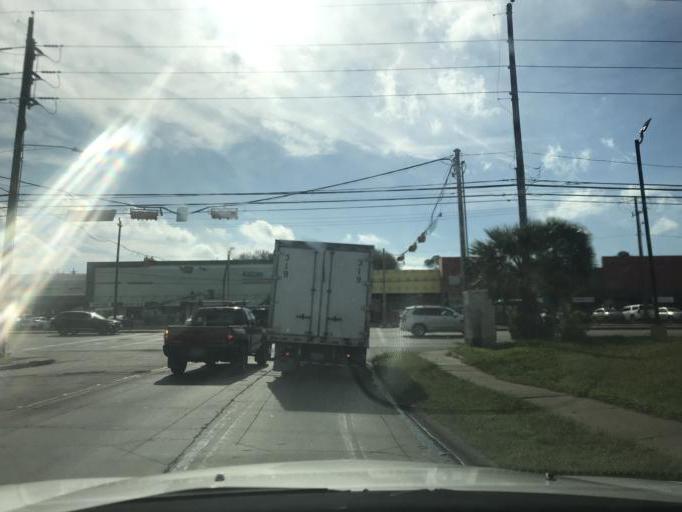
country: US
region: Texas
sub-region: Harris County
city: Piney Point Village
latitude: 29.7381
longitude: -95.4964
